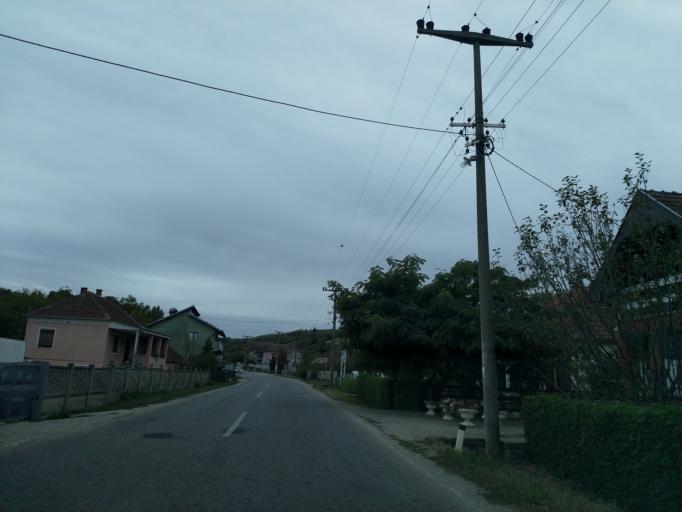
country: RS
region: Central Serbia
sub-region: Pomoravski Okrug
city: Jagodina
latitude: 44.0578
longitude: 21.1813
